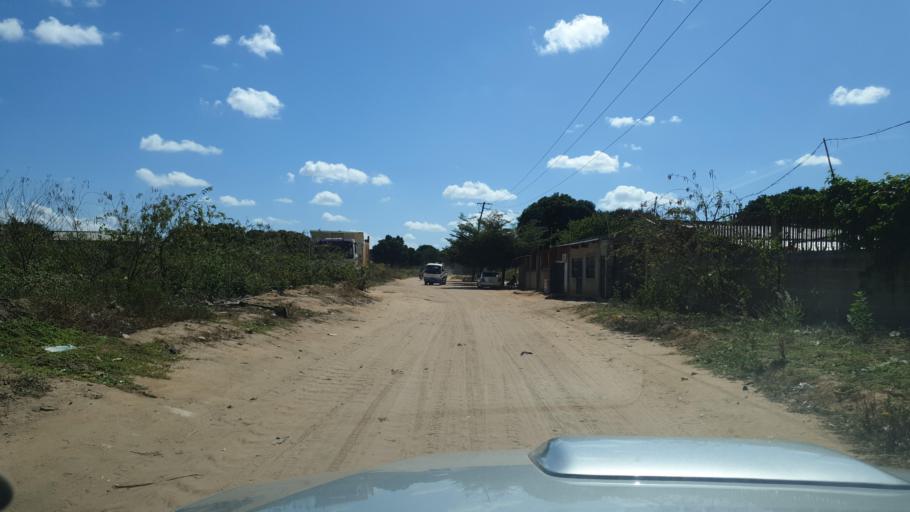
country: MZ
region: Nampula
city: Nampula
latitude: -15.1032
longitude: 39.2060
